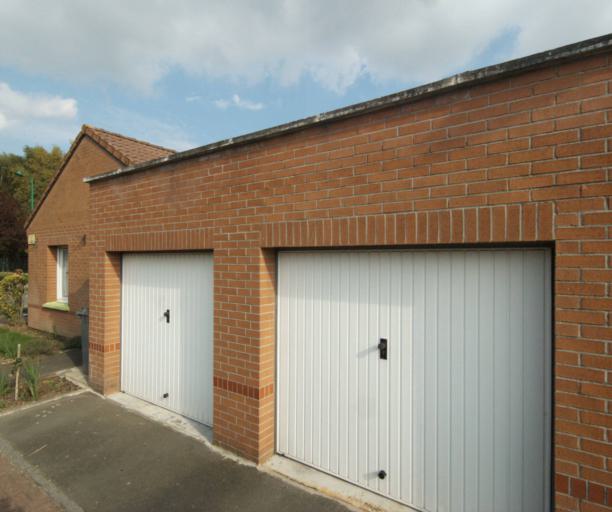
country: FR
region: Nord-Pas-de-Calais
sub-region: Departement du Nord
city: Hallennes-lez-Haubourdin
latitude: 50.6125
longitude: 2.9617
